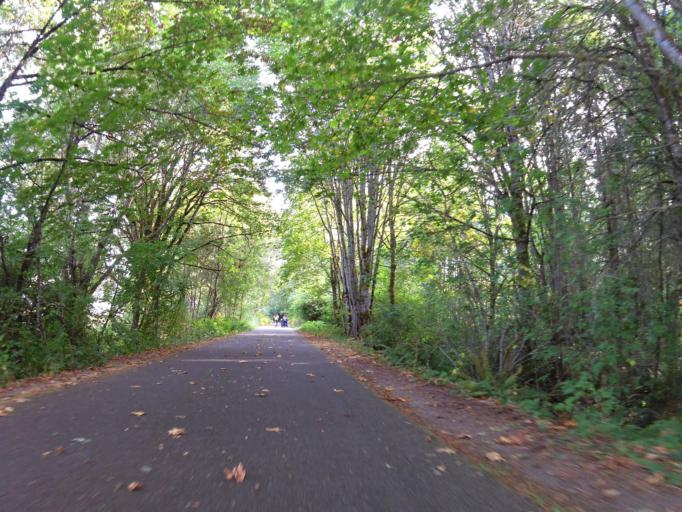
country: US
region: Washington
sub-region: Thurston County
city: Lacey
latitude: 47.0100
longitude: -122.8337
